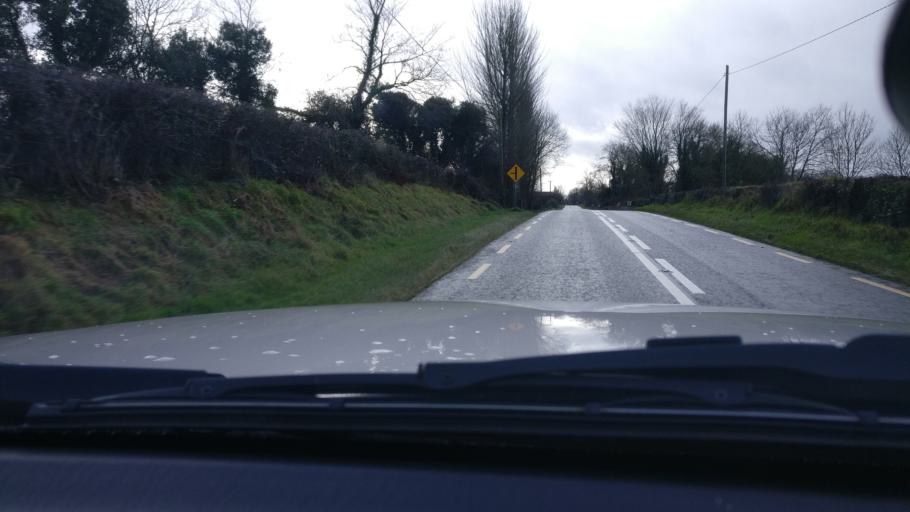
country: IE
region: Leinster
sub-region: An Iarmhi
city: Moate
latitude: 53.6184
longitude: -7.7023
